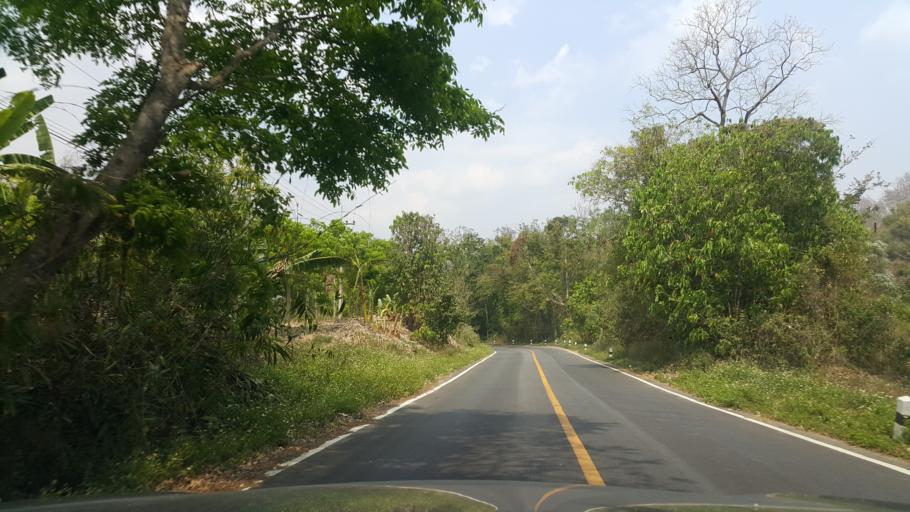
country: TH
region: Lamphun
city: Thung Hua Chang
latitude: 17.9025
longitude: 99.1139
